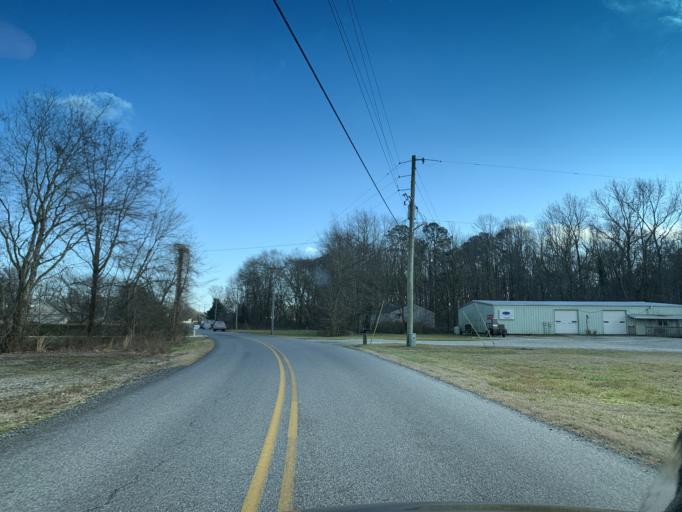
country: US
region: Maryland
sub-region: Worcester County
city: Ocean Pines
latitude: 38.4262
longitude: -75.1722
